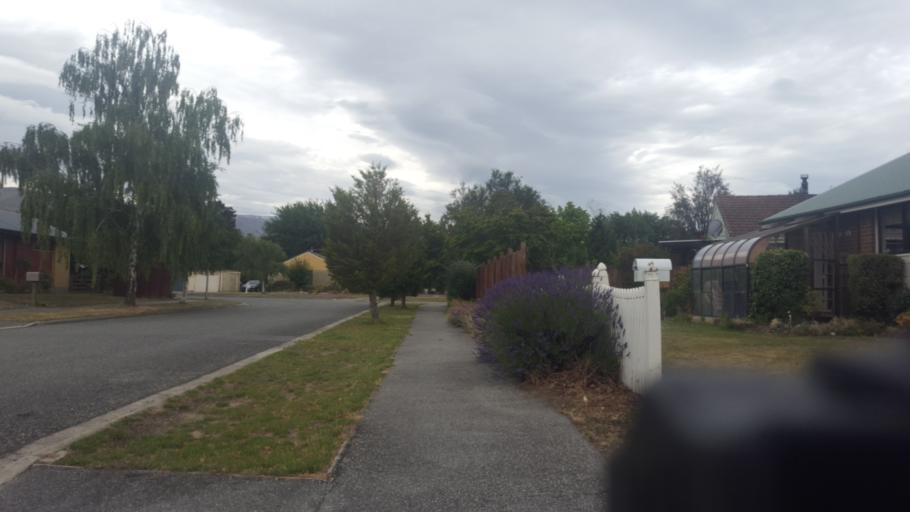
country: NZ
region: Otago
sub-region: Queenstown-Lakes District
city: Wanaka
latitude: -45.0434
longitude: 169.1885
